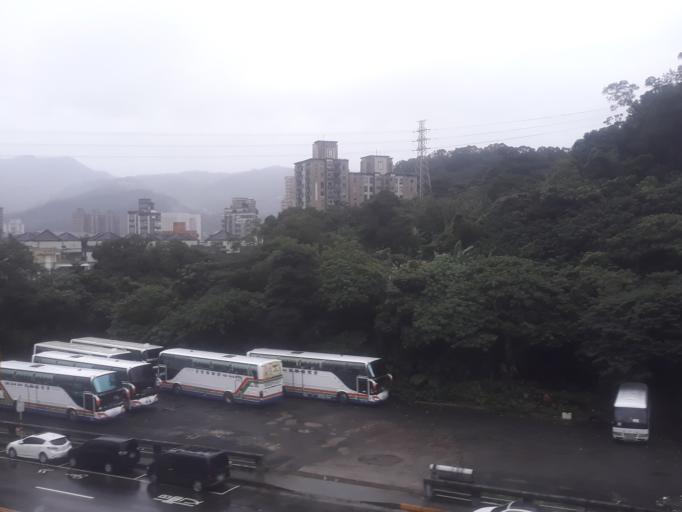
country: TW
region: Taipei
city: Taipei
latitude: 24.9986
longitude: 121.5702
